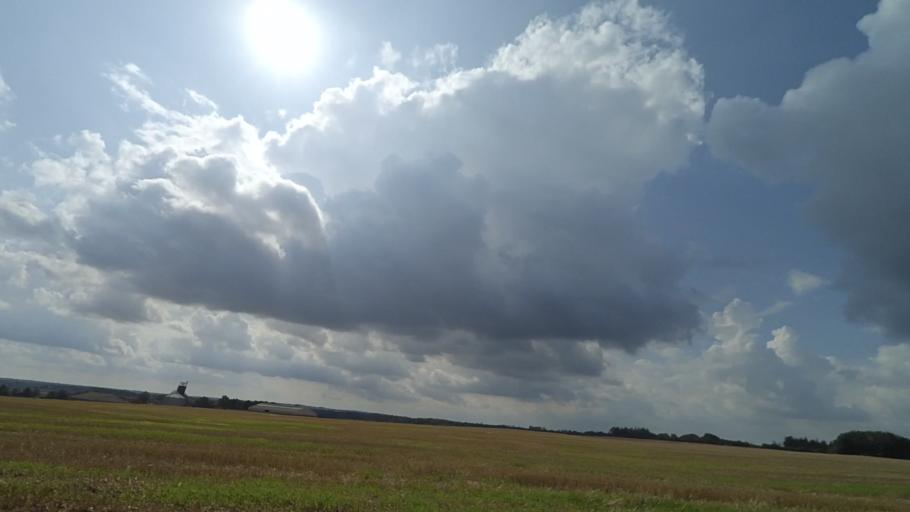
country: DK
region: Central Jutland
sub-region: Norddjurs Kommune
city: Allingabro
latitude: 56.5048
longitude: 10.3694
